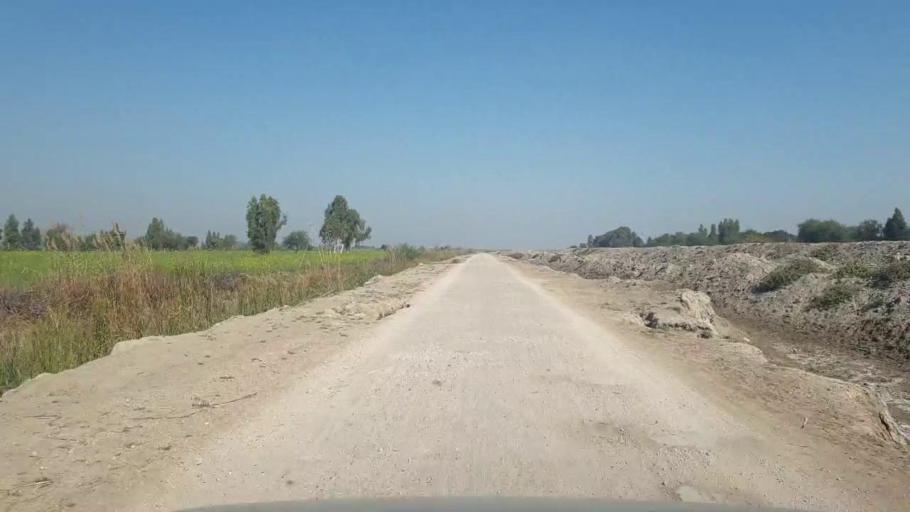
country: PK
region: Sindh
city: Mirwah Gorchani
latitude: 25.3309
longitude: 69.1020
